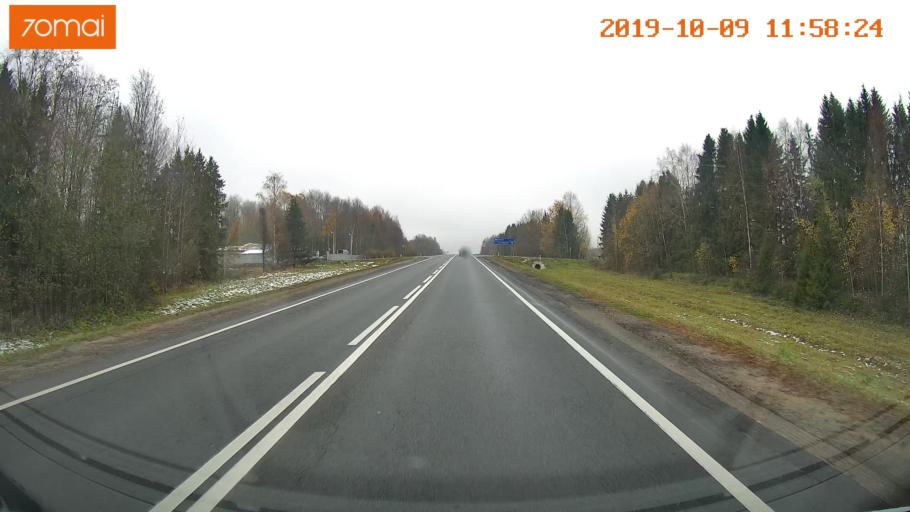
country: RU
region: Vologda
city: Gryazovets
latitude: 58.7185
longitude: 40.2964
